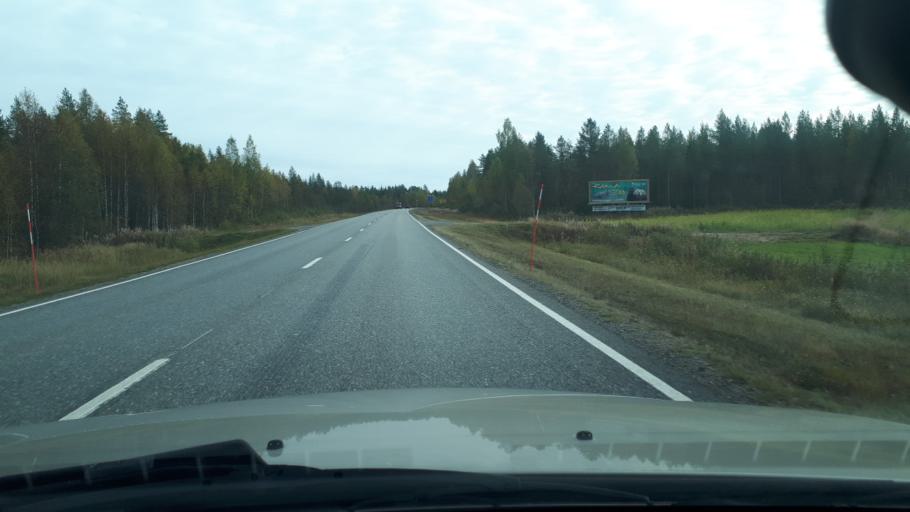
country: FI
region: Lapland
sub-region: Rovaniemi
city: Ranua
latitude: 65.9466
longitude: 26.4494
